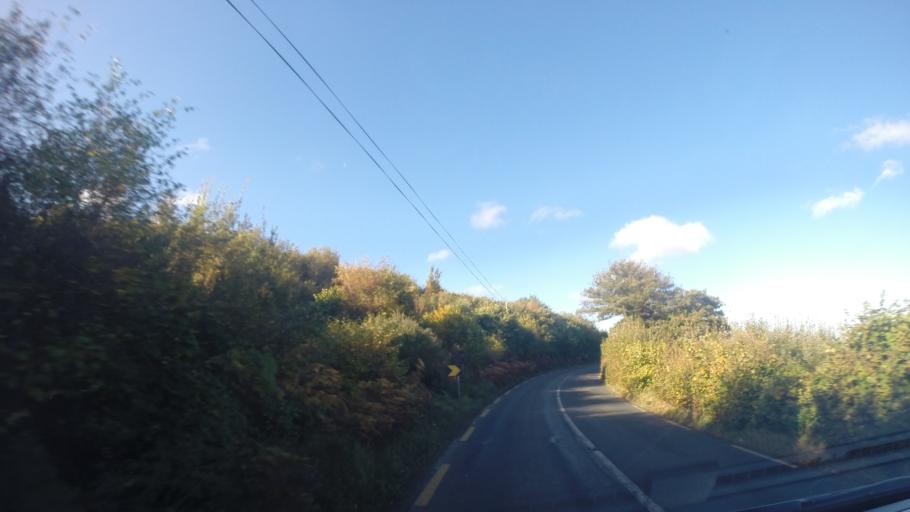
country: IE
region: Ulster
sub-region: County Donegal
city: Dungloe
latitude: 54.8338
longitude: -8.3563
